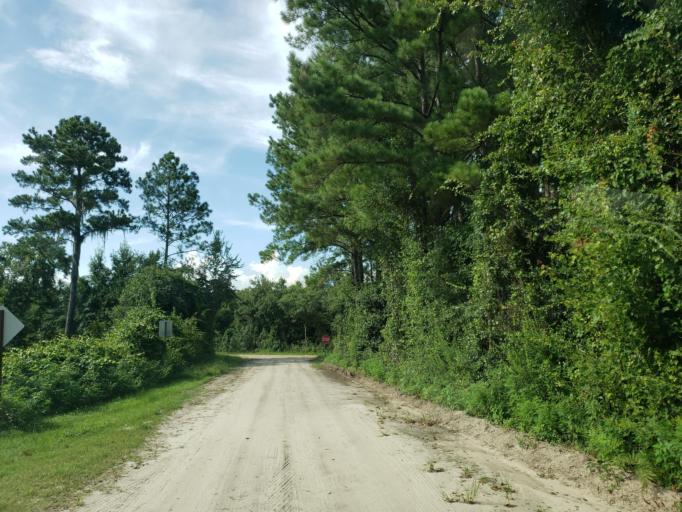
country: US
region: Georgia
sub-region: Echols County
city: Statenville
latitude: 30.6268
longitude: -83.1874
